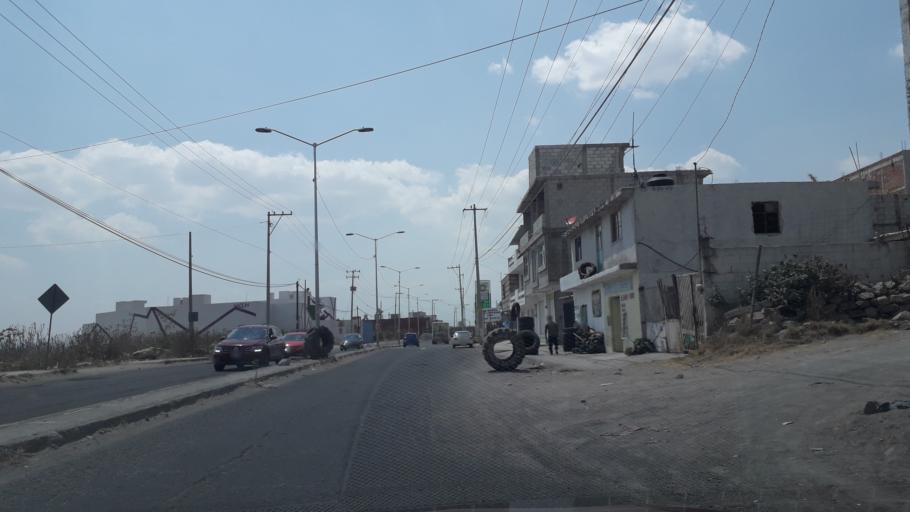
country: MX
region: Puebla
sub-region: Puebla
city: Galaxia la Calera
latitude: 18.9913
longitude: -98.1680
